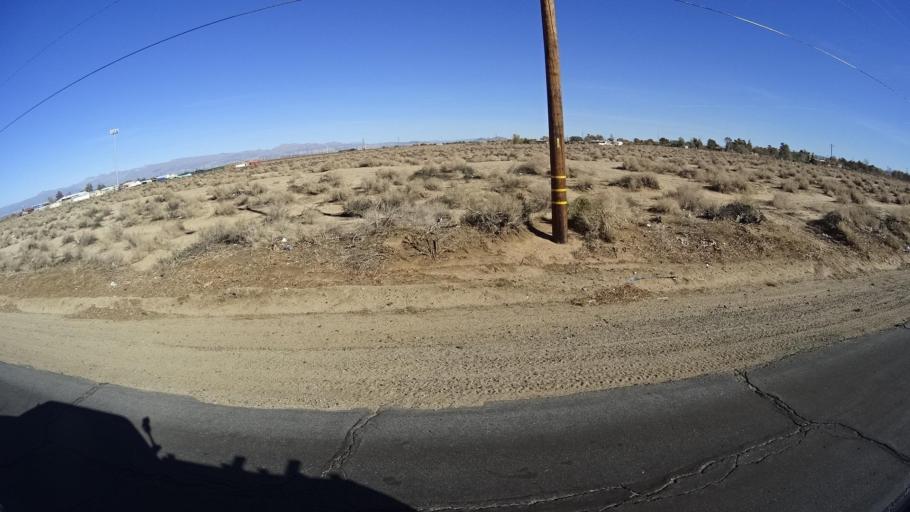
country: US
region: California
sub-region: Kern County
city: Inyokern
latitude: 35.6439
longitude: -117.8114
